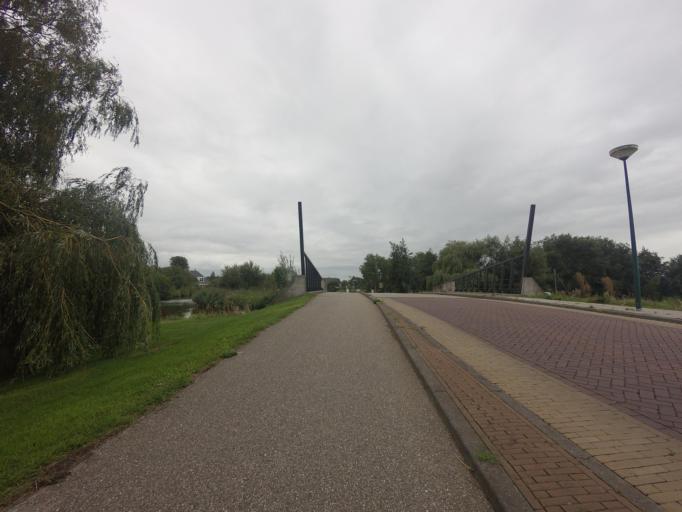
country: NL
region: Friesland
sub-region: Sudwest Fryslan
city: Heeg
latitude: 52.9736
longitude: 5.6058
